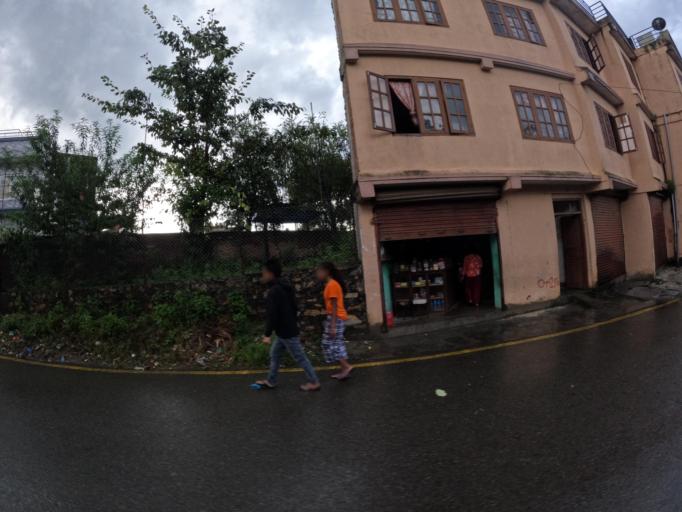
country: NP
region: Central Region
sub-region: Bagmati Zone
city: Kathmandu
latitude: 27.7704
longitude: 85.3318
